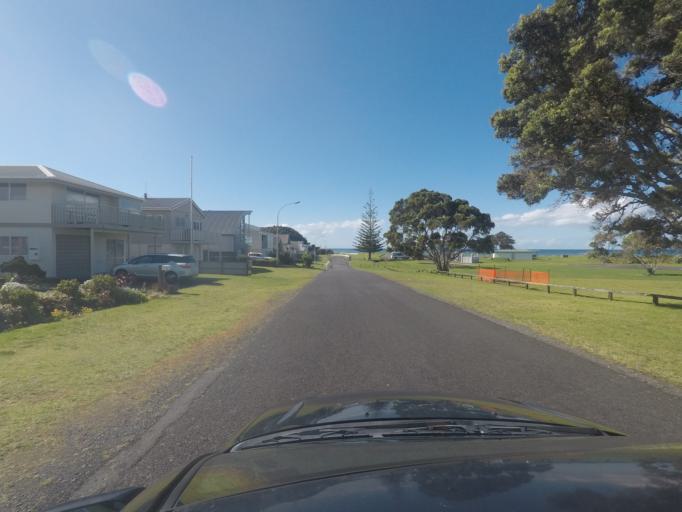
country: NZ
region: Bay of Plenty
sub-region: Western Bay of Plenty District
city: Waihi Beach
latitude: -37.4015
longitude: 175.9389
